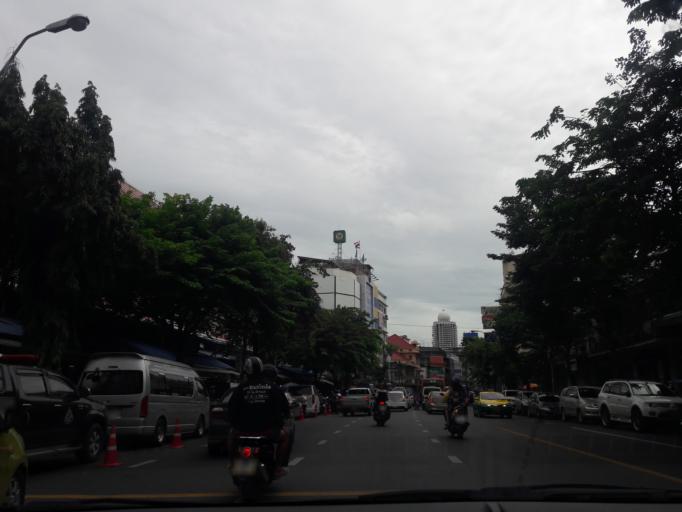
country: TH
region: Bangkok
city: Bangkok
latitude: 13.7470
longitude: 100.5066
